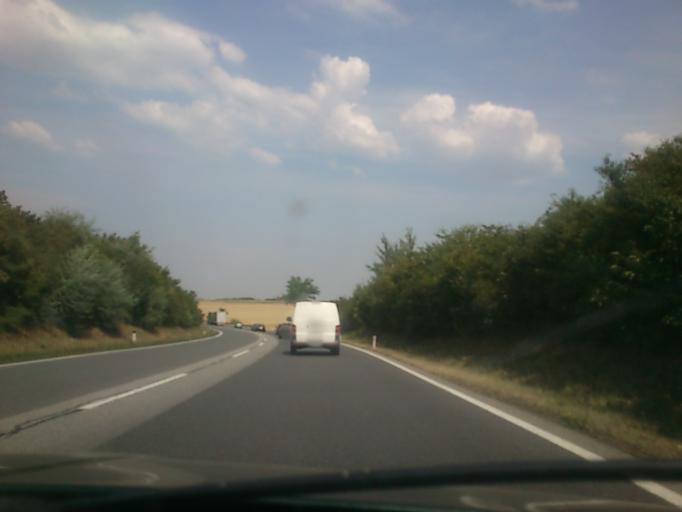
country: AT
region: Lower Austria
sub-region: Politischer Bezirk Mistelbach
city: Herrnbaumgarten
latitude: 48.7072
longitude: 16.6519
